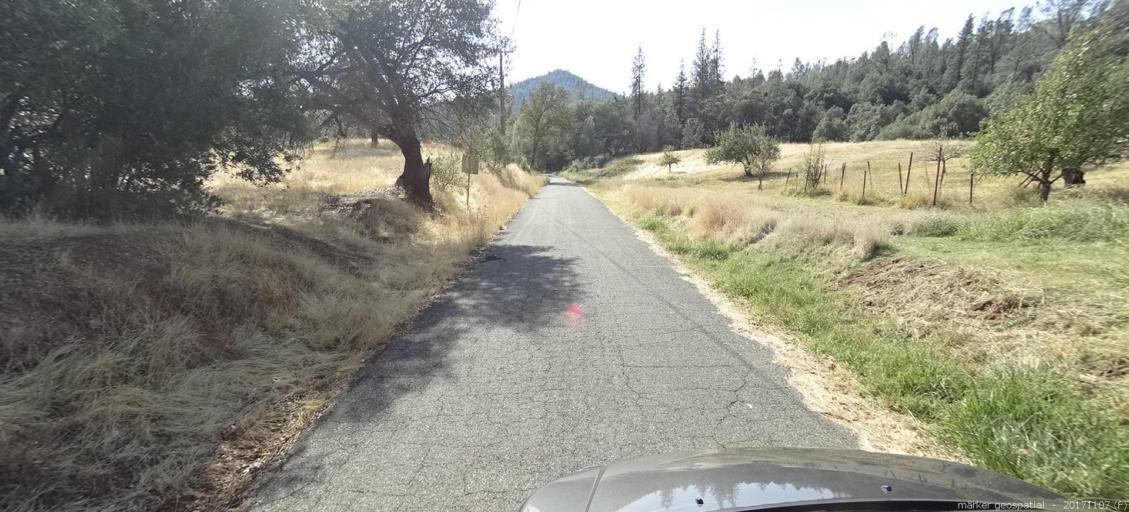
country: US
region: California
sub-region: Shasta County
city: Shasta
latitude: 40.5356
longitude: -122.5580
